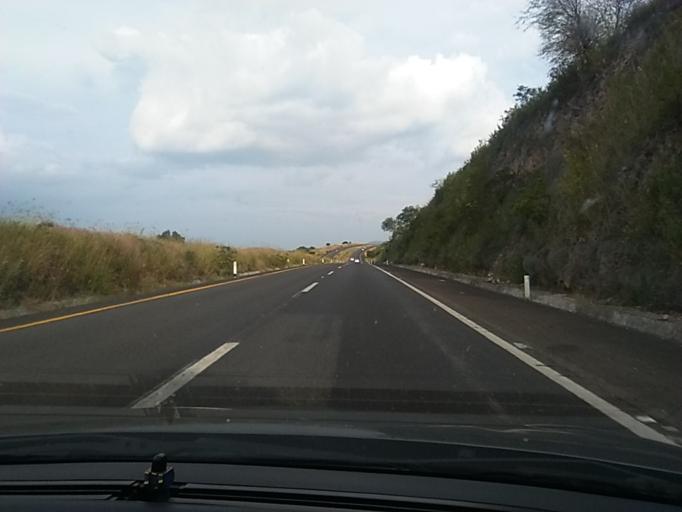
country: MX
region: Mexico
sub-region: Chapultepec
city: Chucandiro
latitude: 19.9038
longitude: -101.2785
